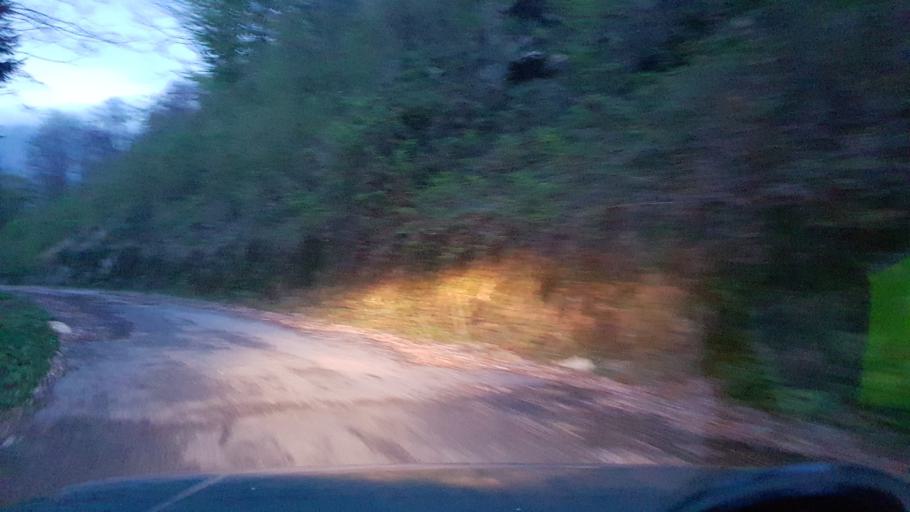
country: IT
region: Friuli Venezia Giulia
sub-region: Provincia di Udine
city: Taipana
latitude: 46.2288
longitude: 13.3557
